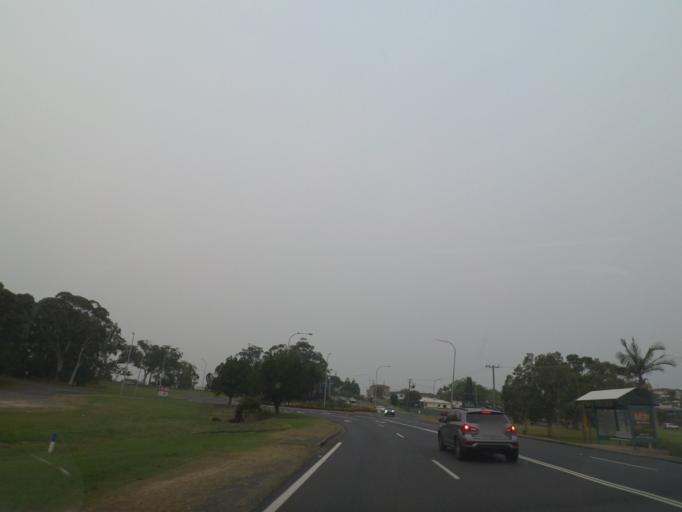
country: AU
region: New South Wales
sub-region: Coffs Harbour
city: Coffs Harbour
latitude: -30.3065
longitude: 153.1221
